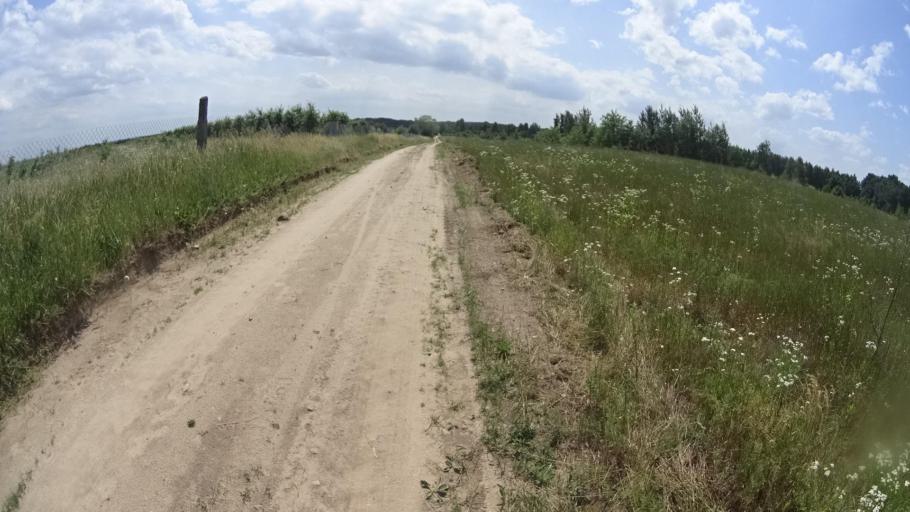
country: PL
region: Masovian Voivodeship
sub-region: Powiat grojecki
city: Goszczyn
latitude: 51.7054
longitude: 20.8277
